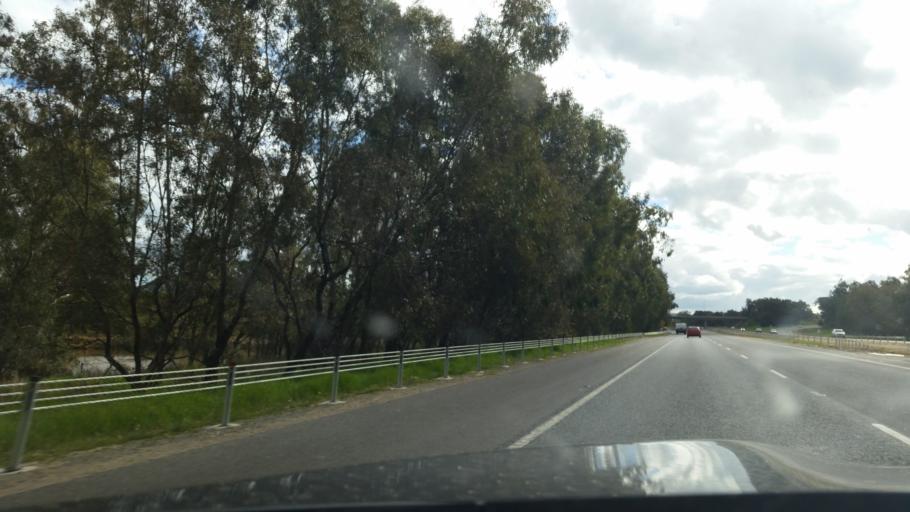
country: AU
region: Victoria
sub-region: Wodonga
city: Wodonga
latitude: -36.1089
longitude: 146.8766
